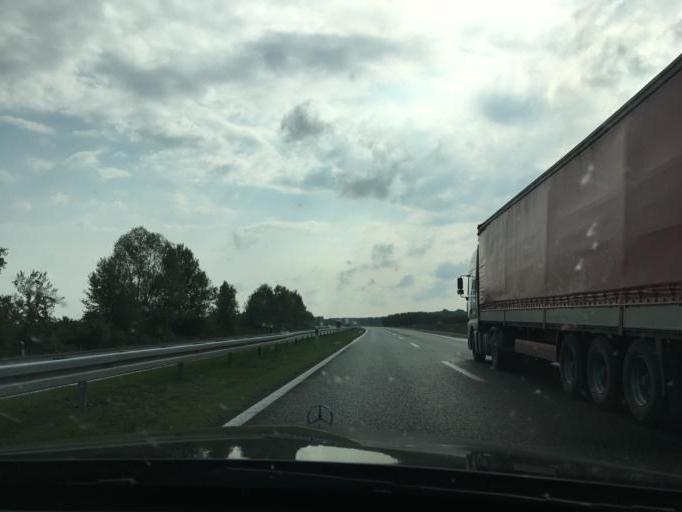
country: HR
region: Brodsko-Posavska
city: Garcin
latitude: 45.1629
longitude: 18.1750
